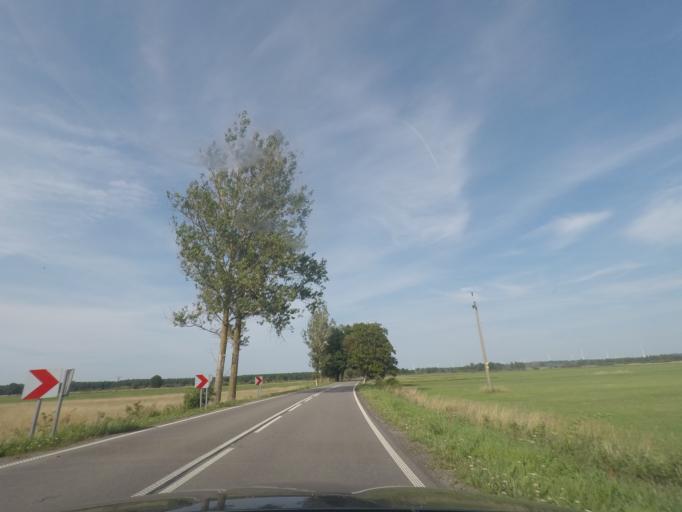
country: PL
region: Pomeranian Voivodeship
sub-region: Powiat leborski
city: Leba
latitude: 54.6501
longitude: 17.5555
